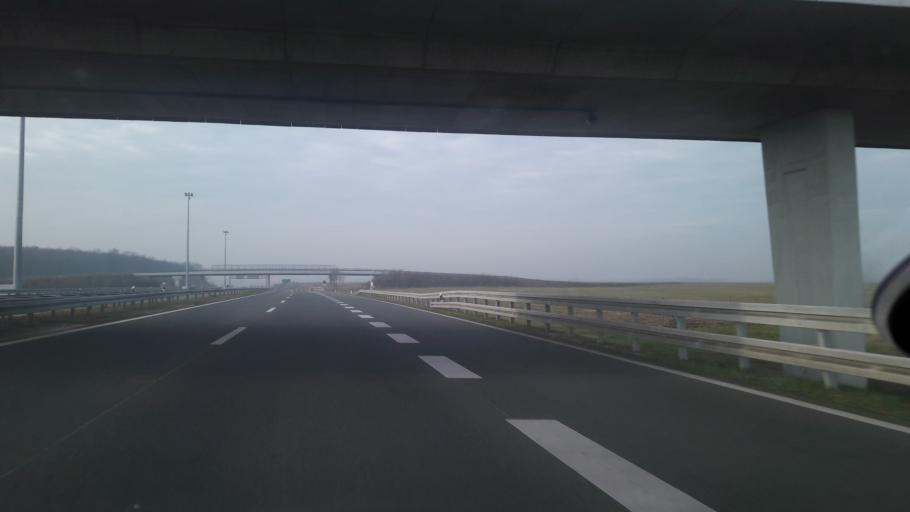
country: HR
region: Osjecko-Baranjska
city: Piskorevci
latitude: 45.3240
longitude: 18.3800
